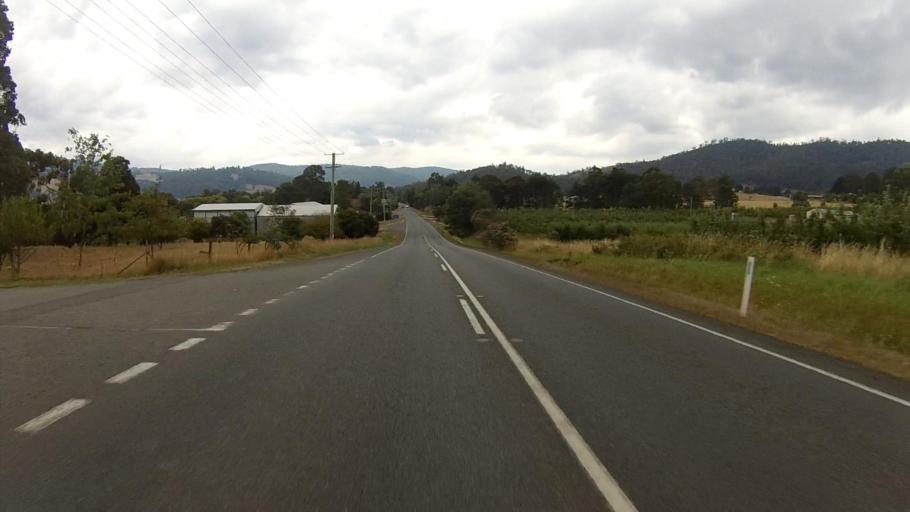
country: AU
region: Tasmania
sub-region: Huon Valley
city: Franklin
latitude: -43.1093
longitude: 147.0356
